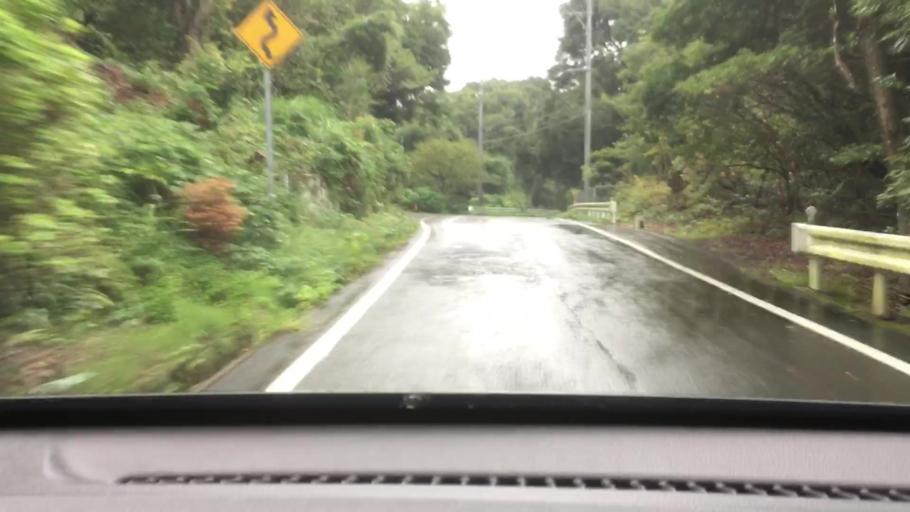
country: JP
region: Nagasaki
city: Togitsu
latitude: 32.8757
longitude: 129.7591
